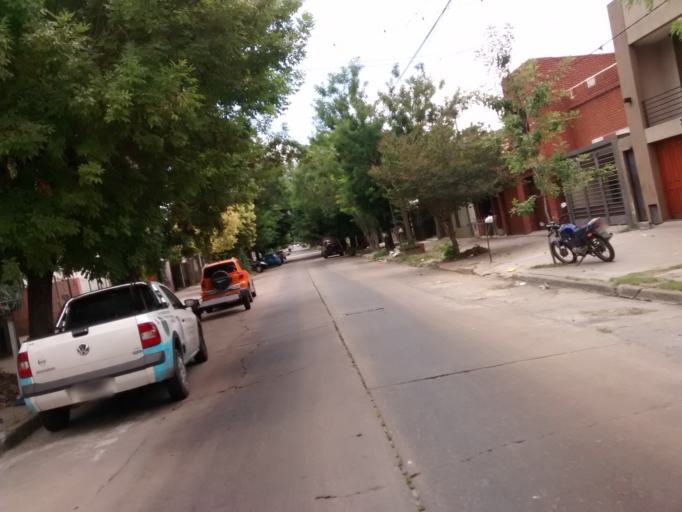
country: AR
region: Buenos Aires
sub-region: Partido de La Plata
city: La Plata
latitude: -34.9450
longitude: -57.9453
